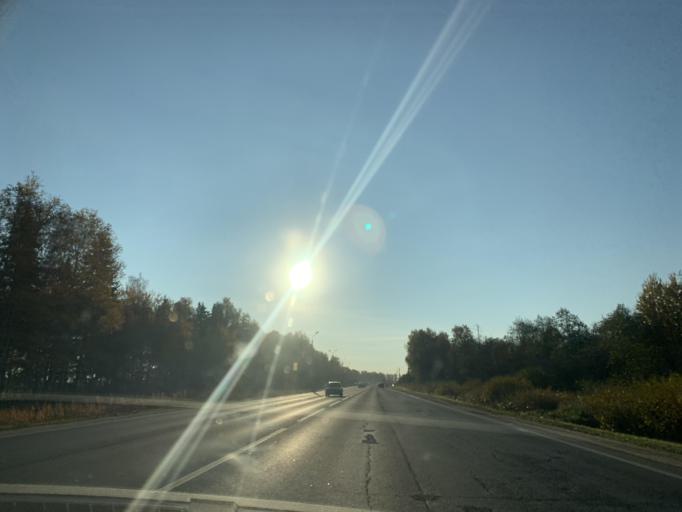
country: RU
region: Jaroslavl
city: Konstantinovskiy
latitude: 57.7436
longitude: 39.7195
